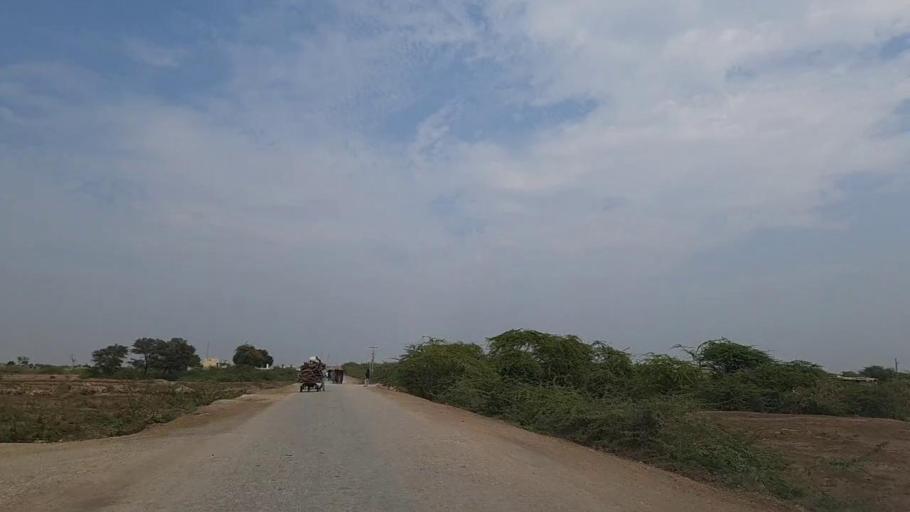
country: PK
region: Sindh
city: Naukot
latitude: 24.9547
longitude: 69.2838
